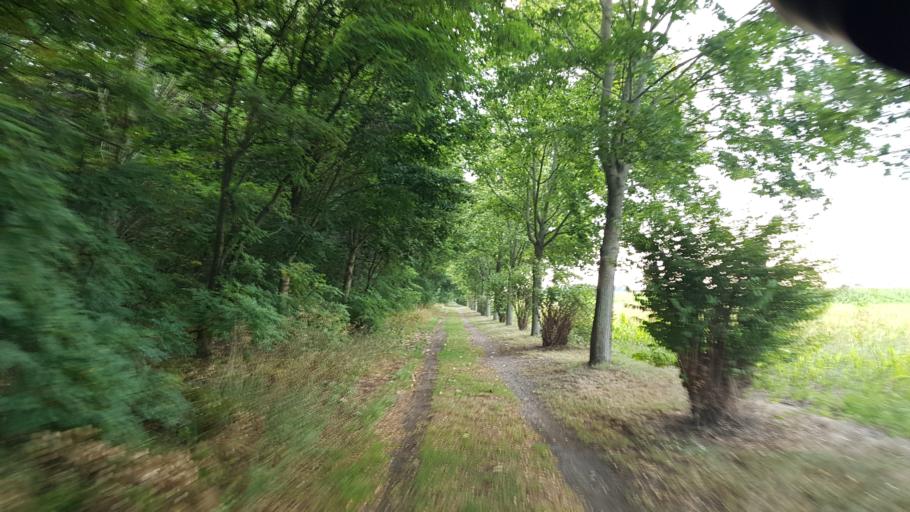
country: DE
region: Brandenburg
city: Tettau
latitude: 51.4230
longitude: 13.7285
